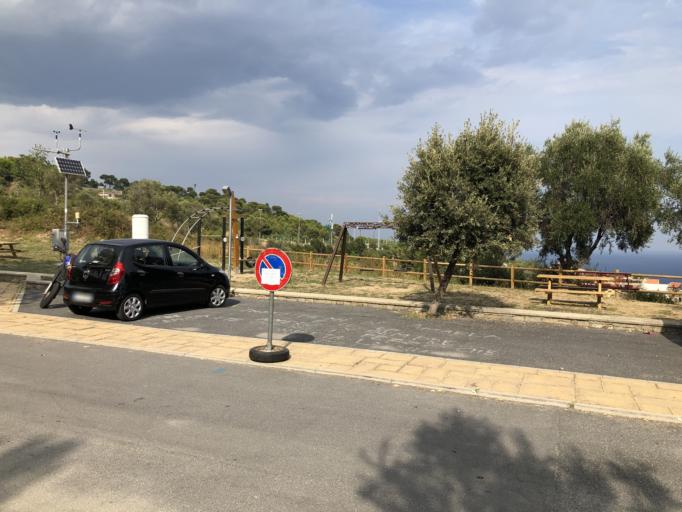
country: IT
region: Liguria
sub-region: Provincia di Imperia
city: Cipressa
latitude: 43.8524
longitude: 7.9284
